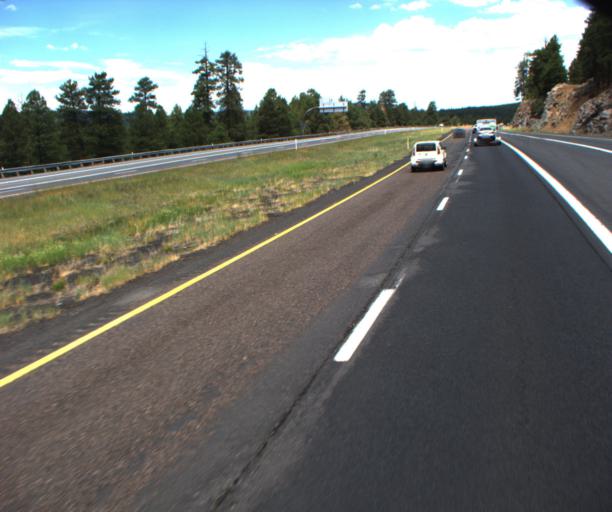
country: US
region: Arizona
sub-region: Coconino County
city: Mountainaire
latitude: 35.0550
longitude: -111.6830
